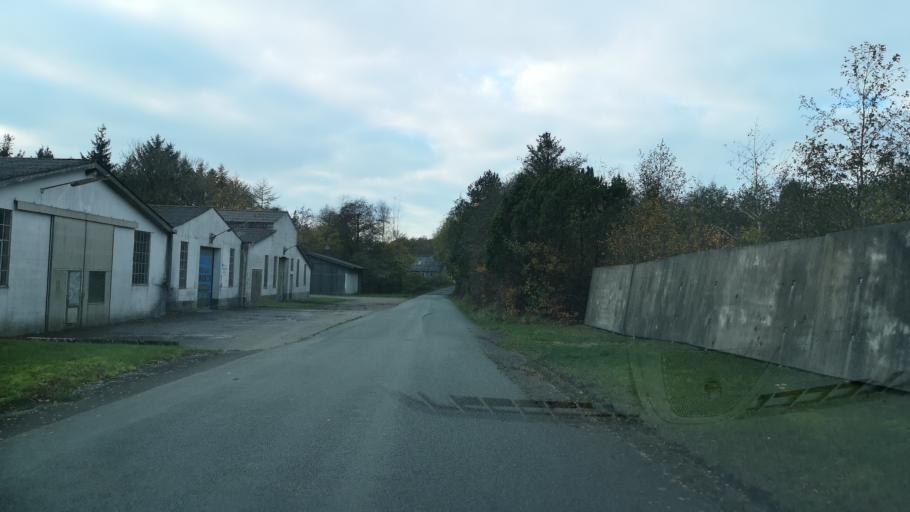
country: DK
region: Central Jutland
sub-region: Ringkobing-Skjern Kommune
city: Videbaek
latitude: 56.0401
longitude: 8.6020
